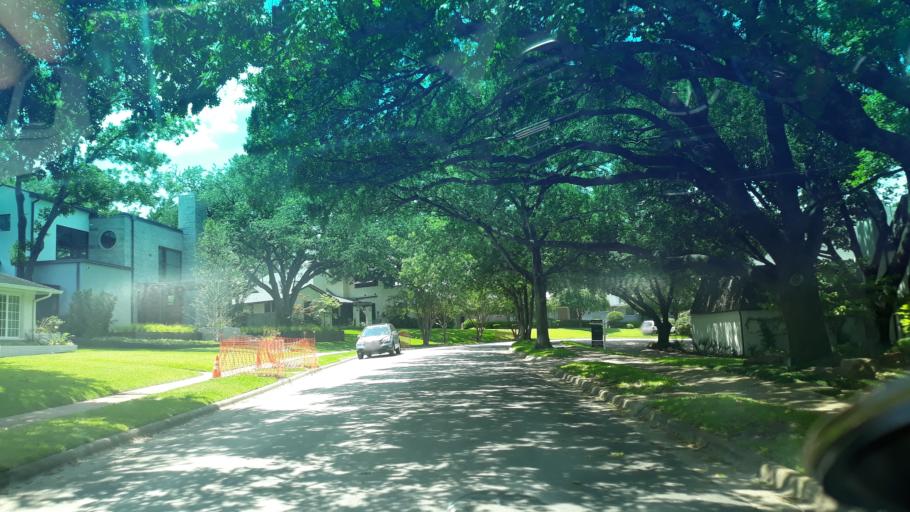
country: US
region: Texas
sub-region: Dallas County
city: Highland Park
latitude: 32.8263
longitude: -96.7413
